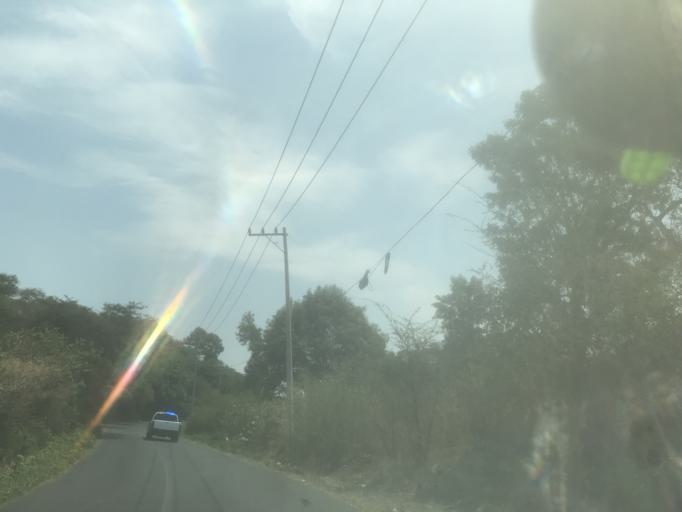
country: MX
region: Mexico
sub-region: Ozumba
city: San Jose Tlacotitlan
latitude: 18.9935
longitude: -98.8041
